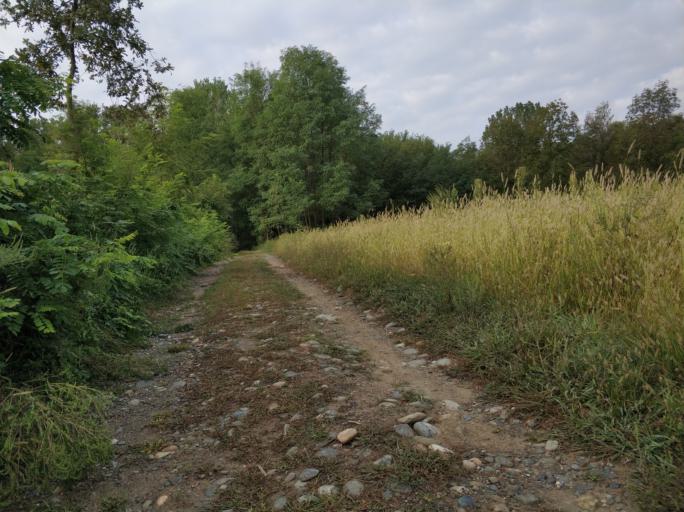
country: IT
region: Piedmont
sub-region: Provincia di Torino
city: Robassomero
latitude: 45.2152
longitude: 7.5702
